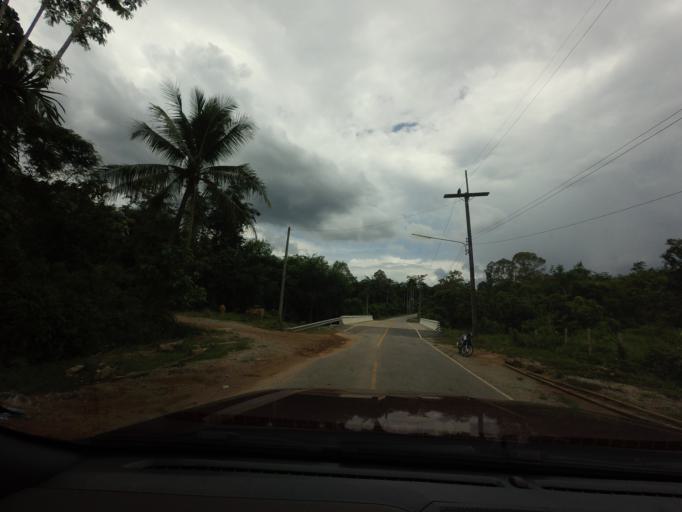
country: TH
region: Narathiwat
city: Sukhirin
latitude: 5.9890
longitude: 101.7062
